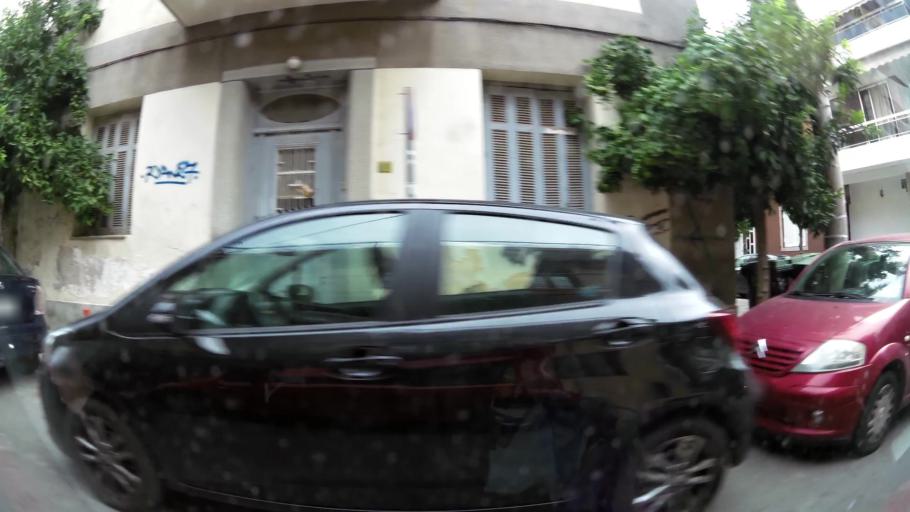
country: GR
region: Attica
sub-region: Nomarchia Athinas
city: Peristeri
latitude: 38.0145
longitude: 23.6917
